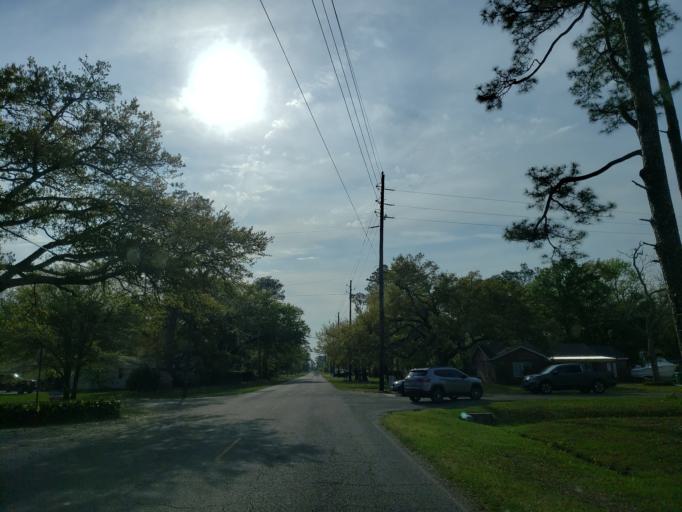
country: US
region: Mississippi
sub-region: Harrison County
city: West Gulfport
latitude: 30.4094
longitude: -89.0455
